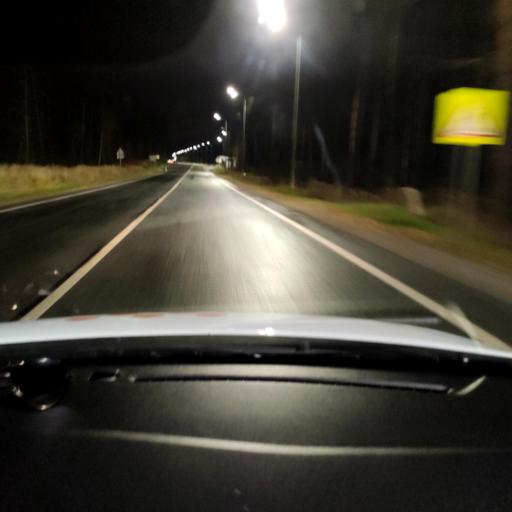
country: RU
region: Tatarstan
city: Stolbishchi
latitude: 55.6336
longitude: 49.1021
